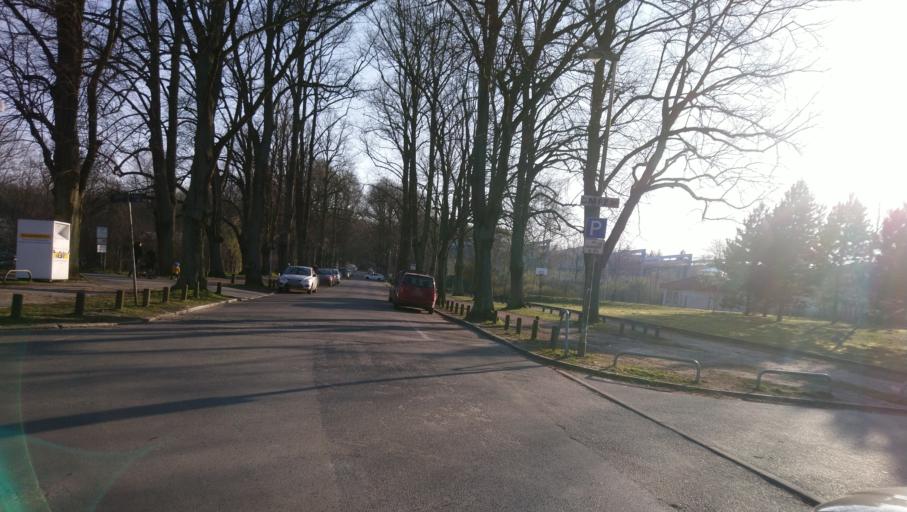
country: DE
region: Mecklenburg-Vorpommern
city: Rostock
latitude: 54.0841
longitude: 12.0995
